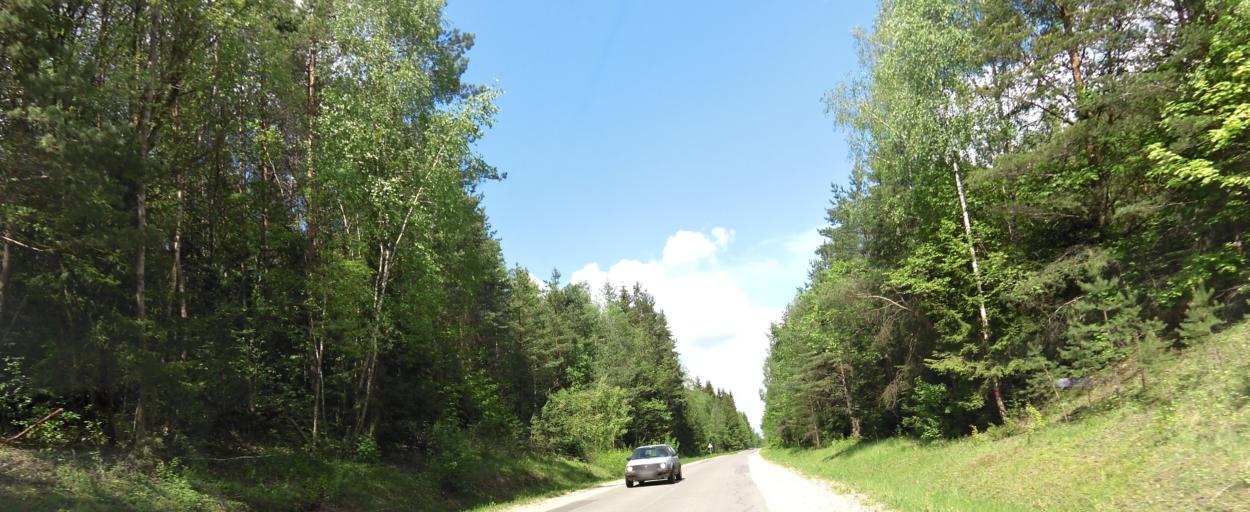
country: LT
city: Trakai
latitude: 54.7043
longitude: 24.9677
